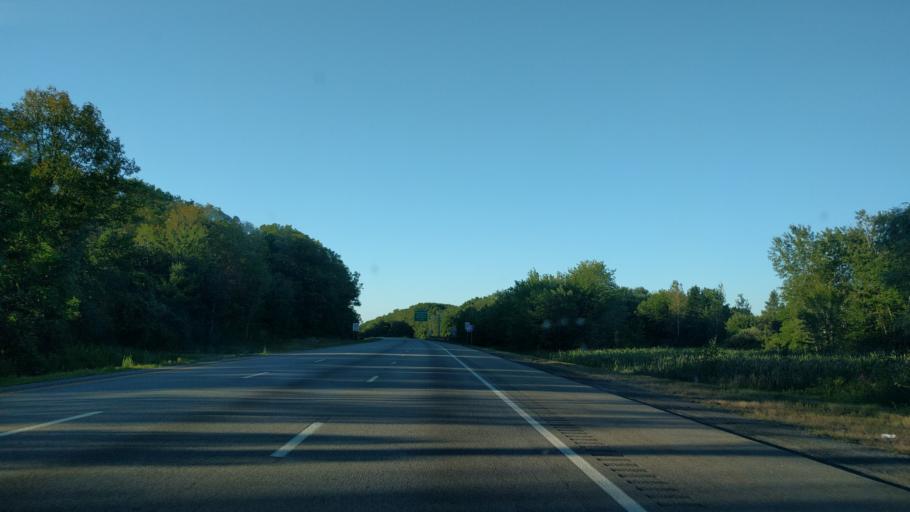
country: US
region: Massachusetts
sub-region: Middlesex County
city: Marlborough
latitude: 42.3325
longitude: -71.5758
